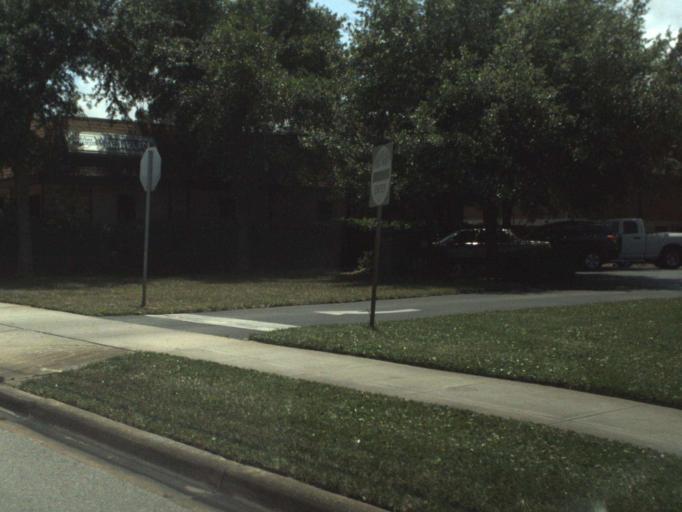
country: US
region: Florida
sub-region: Volusia County
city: Holly Hill
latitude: 29.2528
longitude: -81.0456
